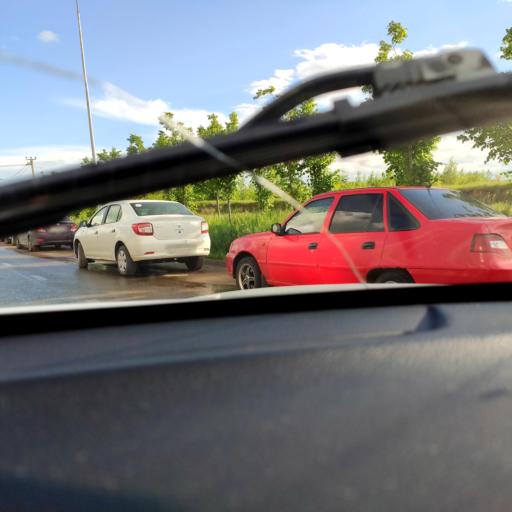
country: RU
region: Tatarstan
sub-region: Gorod Kazan'
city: Kazan
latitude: 55.7879
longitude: 49.2150
